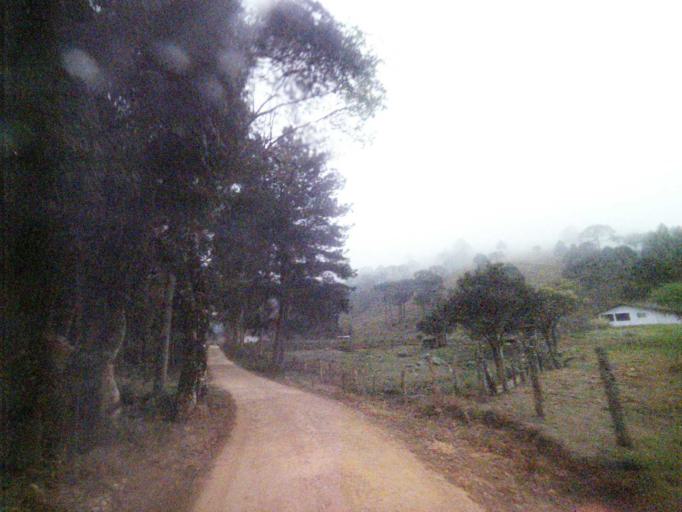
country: BR
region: Santa Catarina
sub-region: Anitapolis
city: Anitapolis
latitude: -27.8013
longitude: -49.1400
